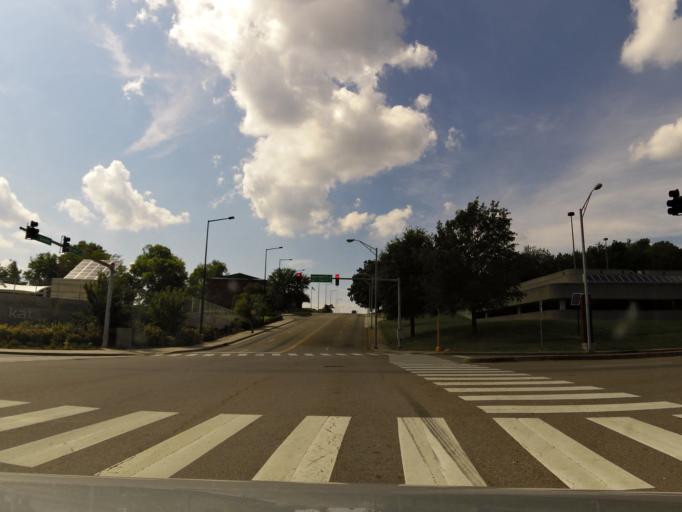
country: US
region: Tennessee
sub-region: Knox County
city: Knoxville
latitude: 35.9654
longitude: -83.9128
